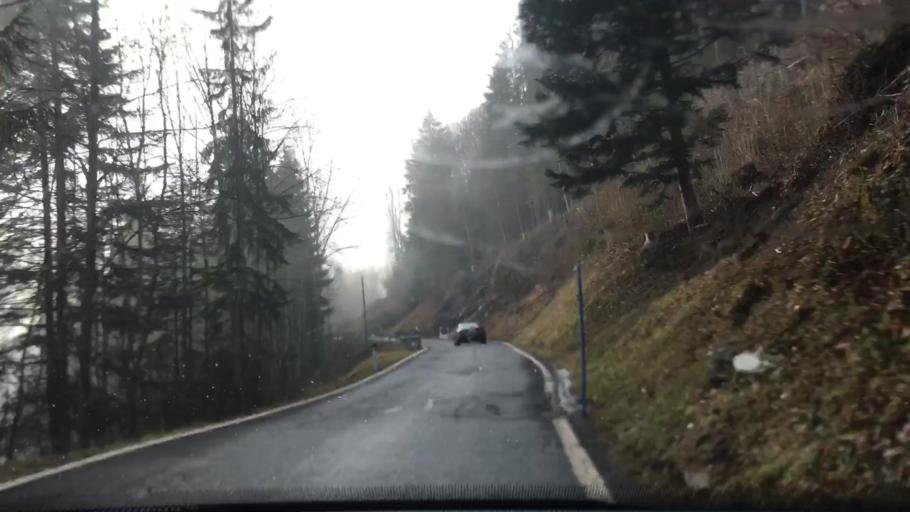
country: CH
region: Valais
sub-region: Monthey District
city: Troistorrents
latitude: 46.2232
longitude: 6.9007
